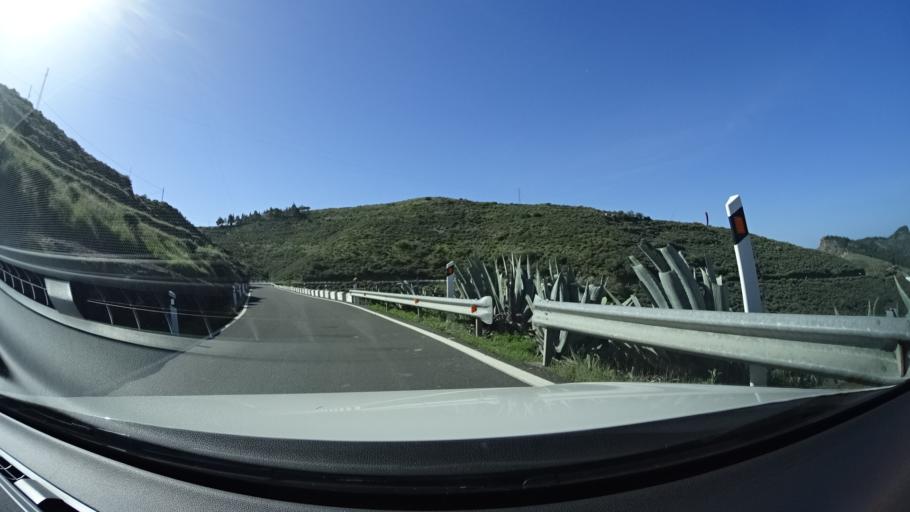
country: ES
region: Canary Islands
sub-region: Provincia de Las Palmas
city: Artenara
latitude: 28.0231
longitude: -15.6430
